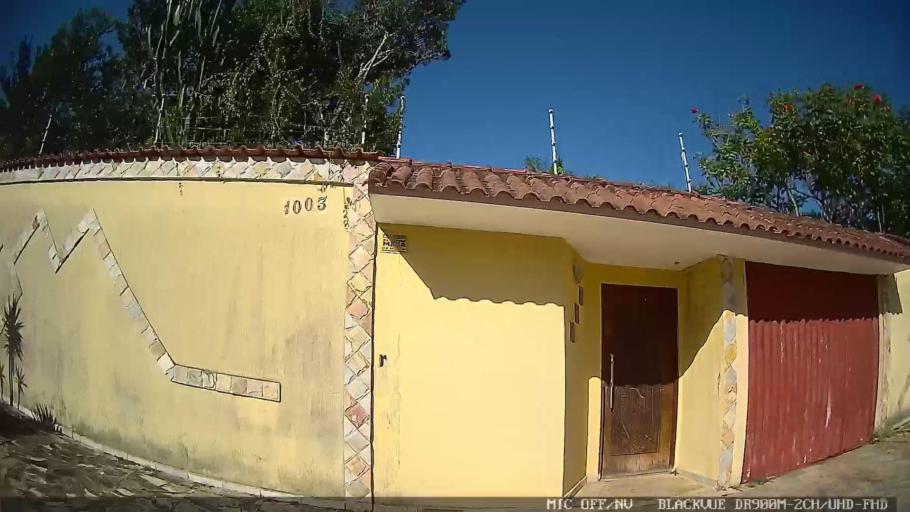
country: BR
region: Sao Paulo
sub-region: Peruibe
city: Peruibe
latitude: -24.2772
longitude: -46.9531
